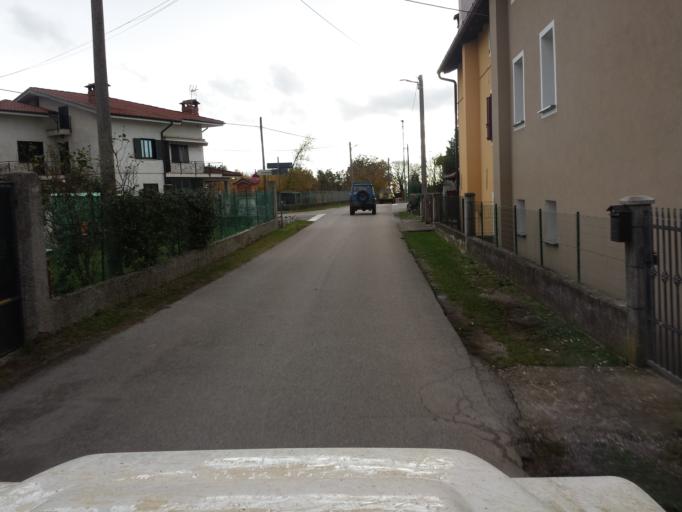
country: IT
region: Friuli Venezia Giulia
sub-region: Provincia di Gorizia
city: Doberdo del Lago
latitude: 45.8757
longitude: 13.5340
